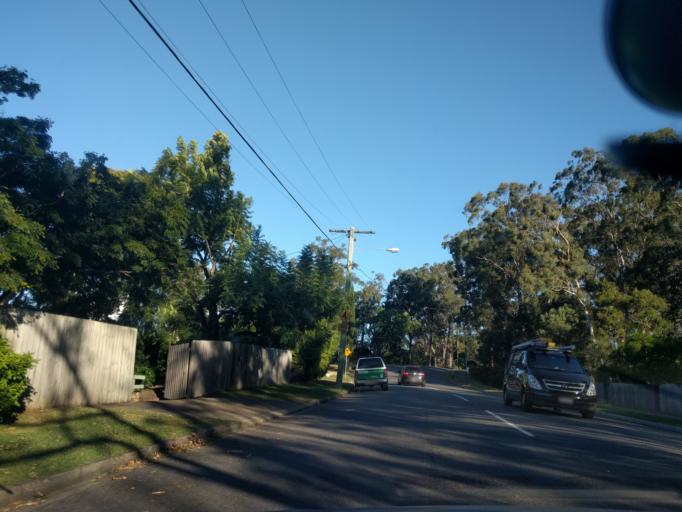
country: AU
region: Queensland
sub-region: Brisbane
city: Kenmore Hills
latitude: -27.5202
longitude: 152.9559
